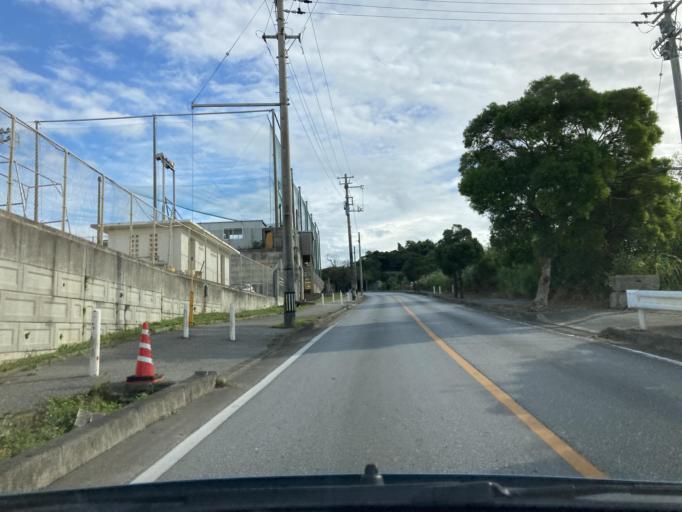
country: JP
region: Okinawa
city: Itoman
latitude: 26.1296
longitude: 127.7103
